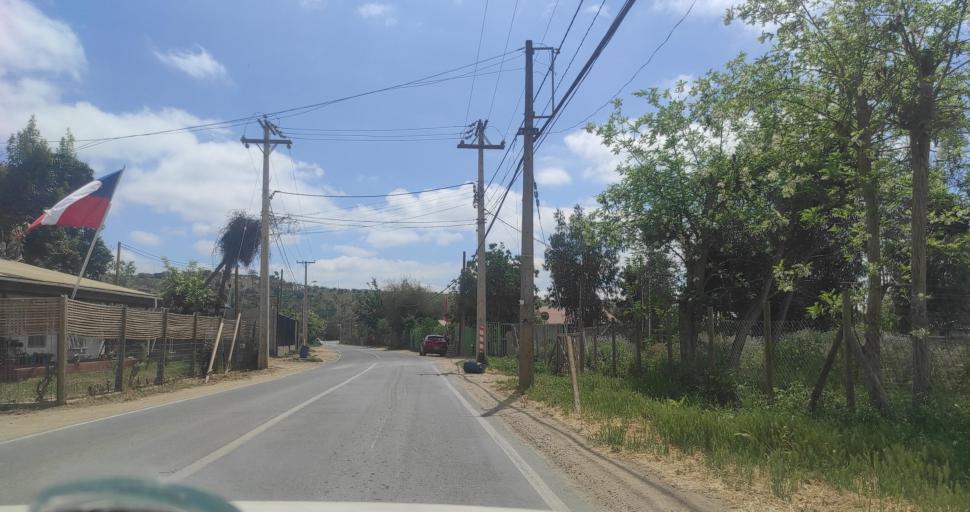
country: CL
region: Valparaiso
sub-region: Provincia de Marga Marga
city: Limache
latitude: -33.0326
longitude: -71.2445
